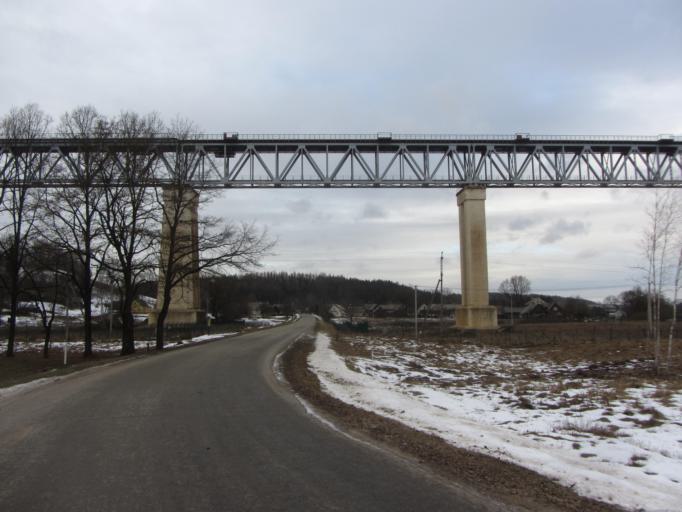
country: LT
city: Raseiniai
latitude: 55.5051
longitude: 23.0863
